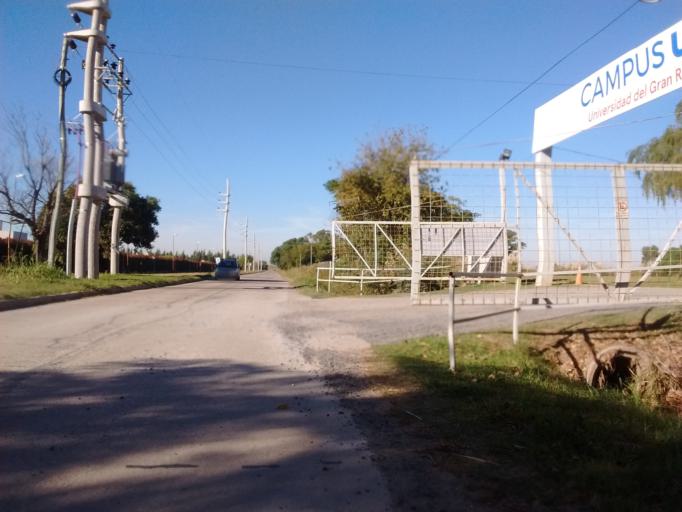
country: AR
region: Santa Fe
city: Funes
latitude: -32.9342
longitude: -60.8120
